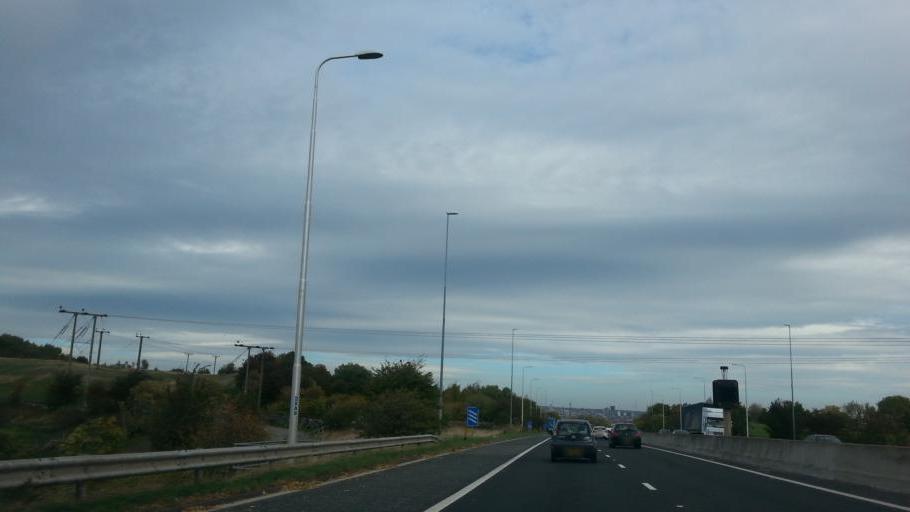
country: GB
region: England
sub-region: City and Borough of Leeds
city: Morley
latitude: 53.7686
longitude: -1.5919
